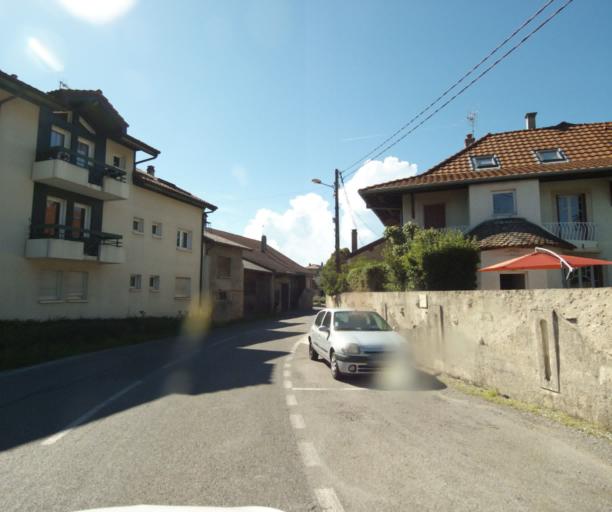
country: FR
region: Rhone-Alpes
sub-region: Departement de la Haute-Savoie
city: Sciez
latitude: 46.3273
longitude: 6.3792
